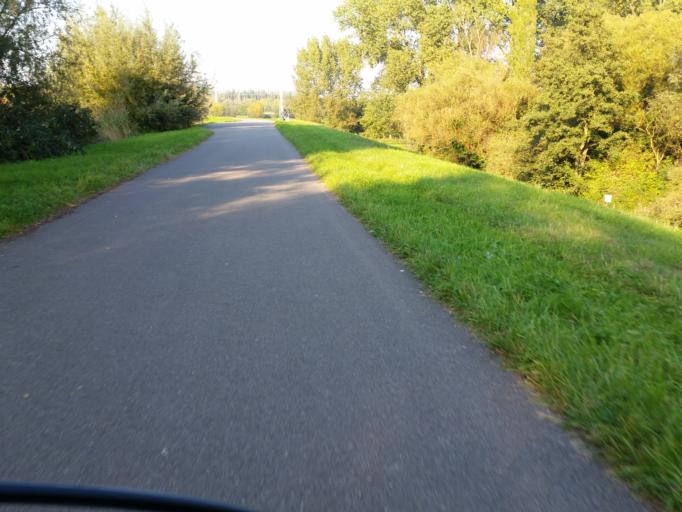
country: BE
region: Flanders
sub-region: Provincie Antwerpen
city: Niel
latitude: 51.1136
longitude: 4.3138
